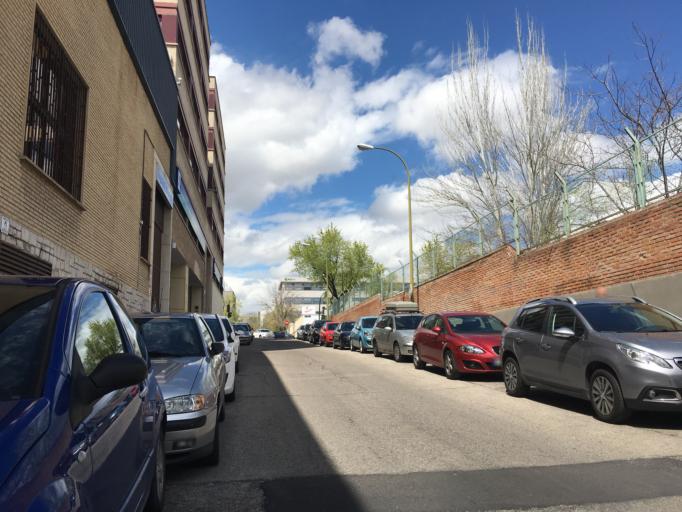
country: ES
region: Madrid
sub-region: Provincia de Madrid
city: San Blas
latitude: 40.4346
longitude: -3.6263
